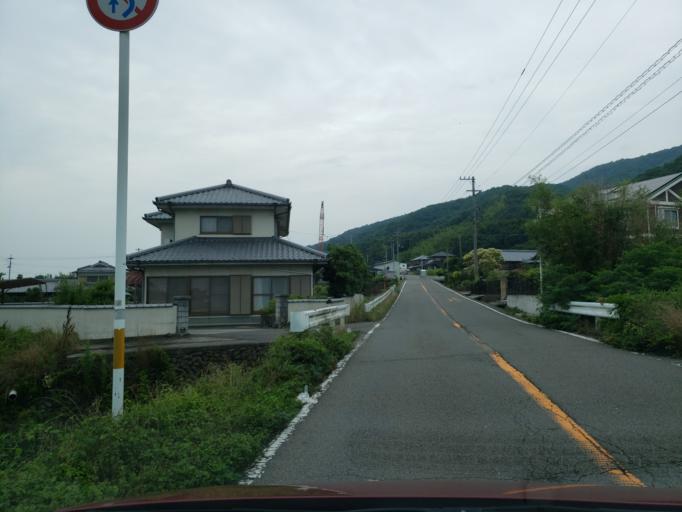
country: JP
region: Tokushima
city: Kamojimacho-jogejima
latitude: 34.1053
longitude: 134.2614
